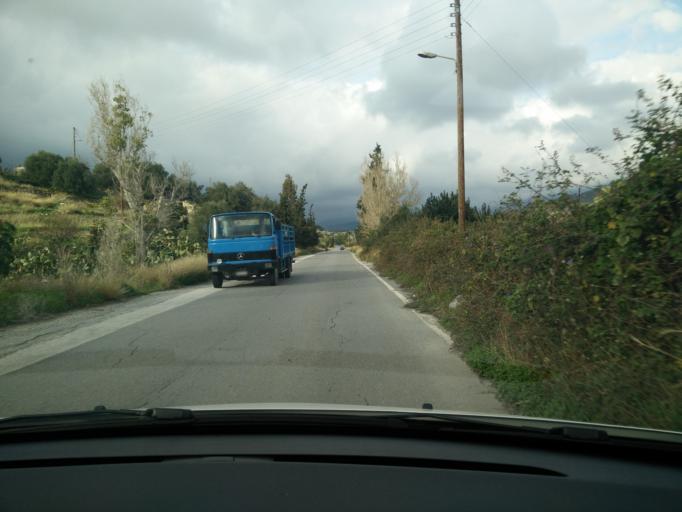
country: GR
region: Crete
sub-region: Nomos Lasithiou
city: Gra Liyia
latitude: 35.0100
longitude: 25.5836
